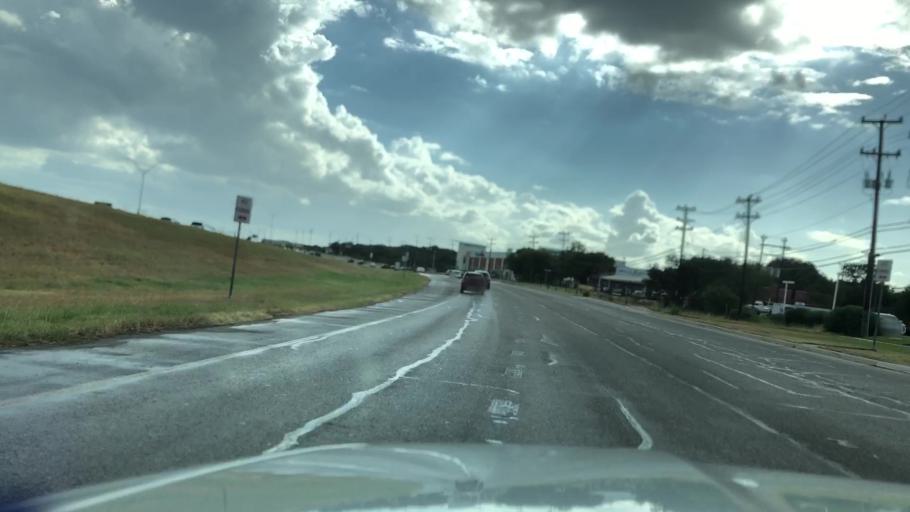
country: US
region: Texas
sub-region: Bexar County
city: Helotes
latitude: 29.5875
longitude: -98.6329
